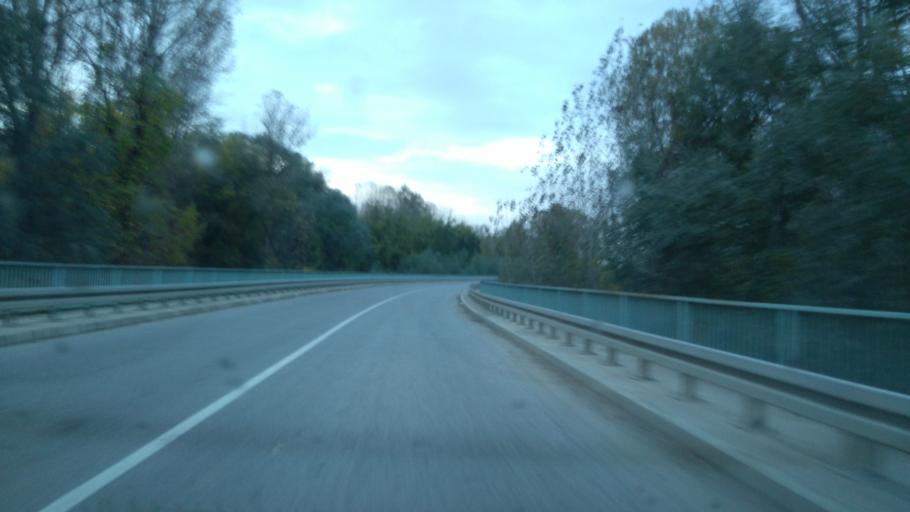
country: RS
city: Mol
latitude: 45.7839
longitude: 20.1525
